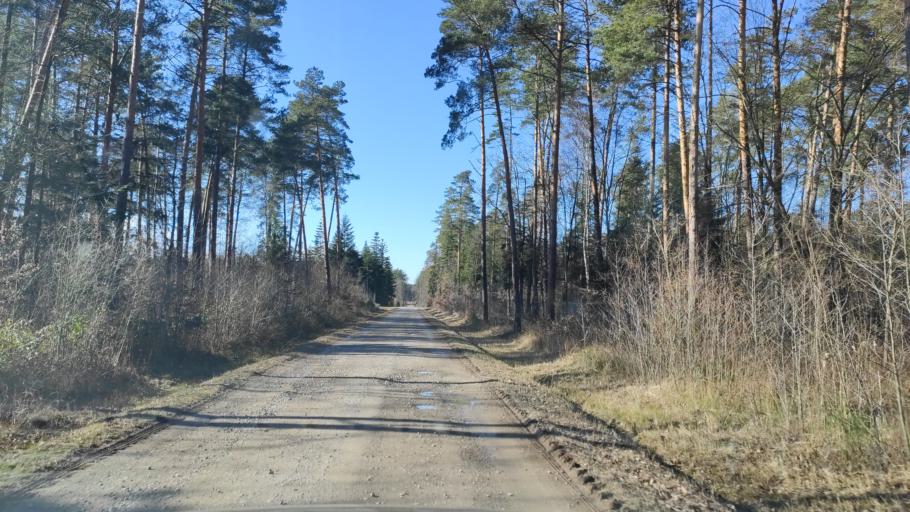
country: PL
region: Masovian Voivodeship
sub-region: Powiat radomski
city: Jedlnia-Letnisko
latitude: 51.4697
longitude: 21.3063
